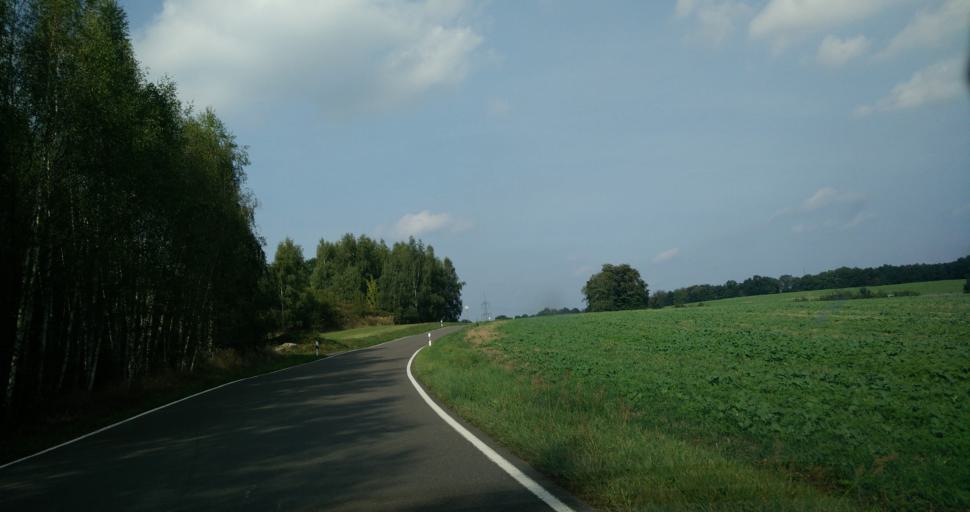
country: DE
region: Saxony
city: Colditz
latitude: 51.1003
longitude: 12.7959
